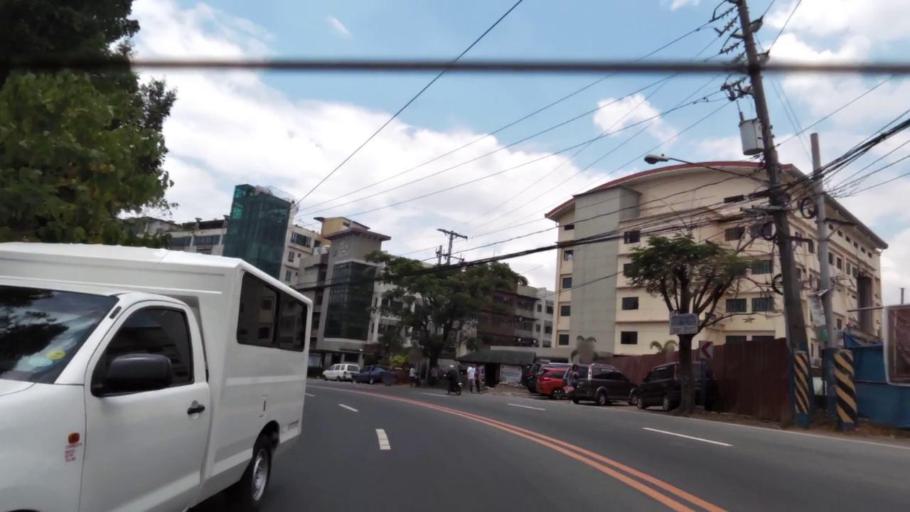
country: PH
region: Calabarzon
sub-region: Province of Rizal
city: Antipolo
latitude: 14.6187
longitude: 121.1523
